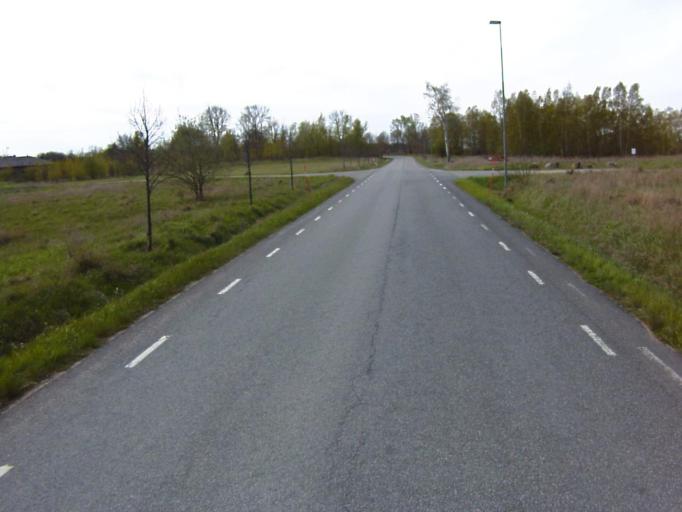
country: SE
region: Skane
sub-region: Kristianstads Kommun
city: Kristianstad
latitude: 56.0522
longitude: 14.1447
